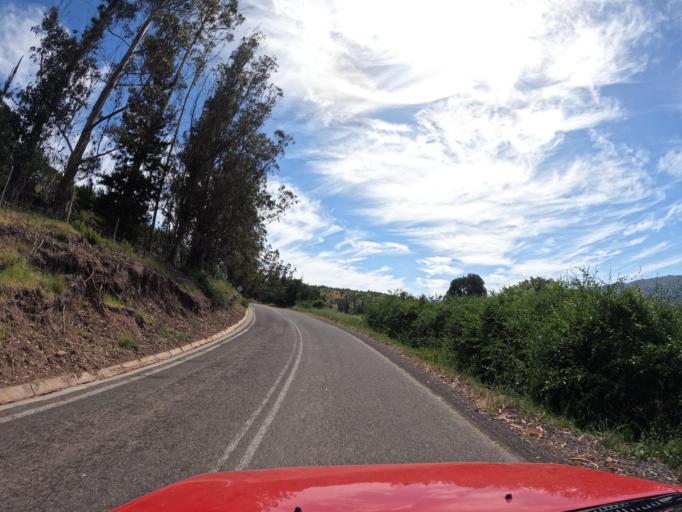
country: CL
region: Maule
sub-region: Provincia de Talca
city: Talca
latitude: -35.0059
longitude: -71.9785
